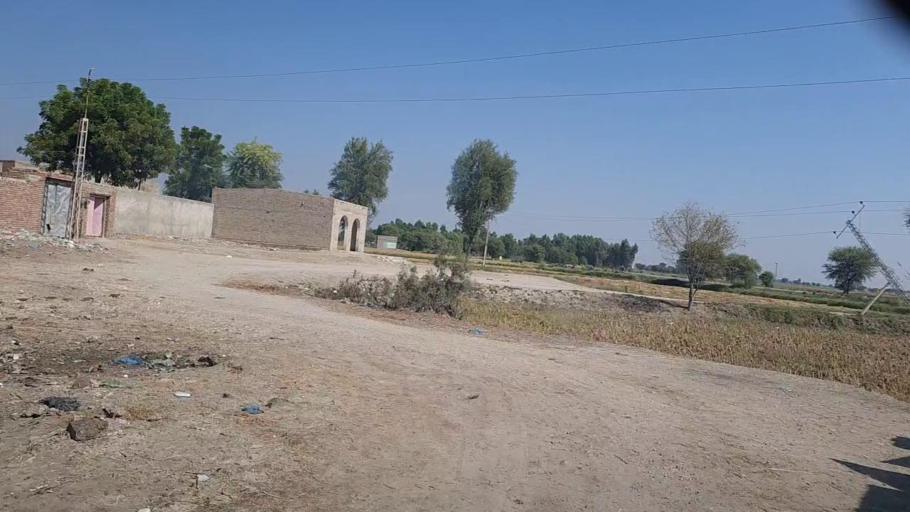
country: PK
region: Sindh
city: Thul
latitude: 28.2184
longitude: 68.7552
